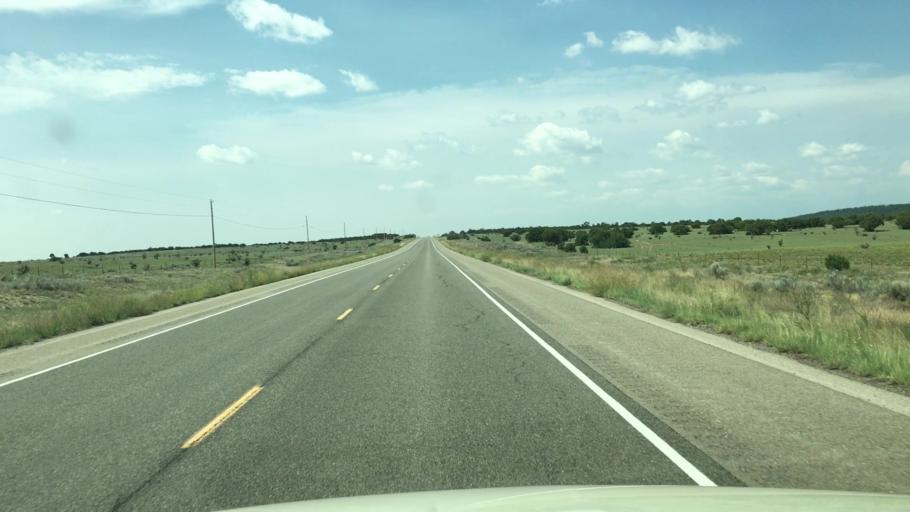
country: US
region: New Mexico
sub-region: Torrance County
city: Moriarty
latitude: 35.0354
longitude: -105.6793
